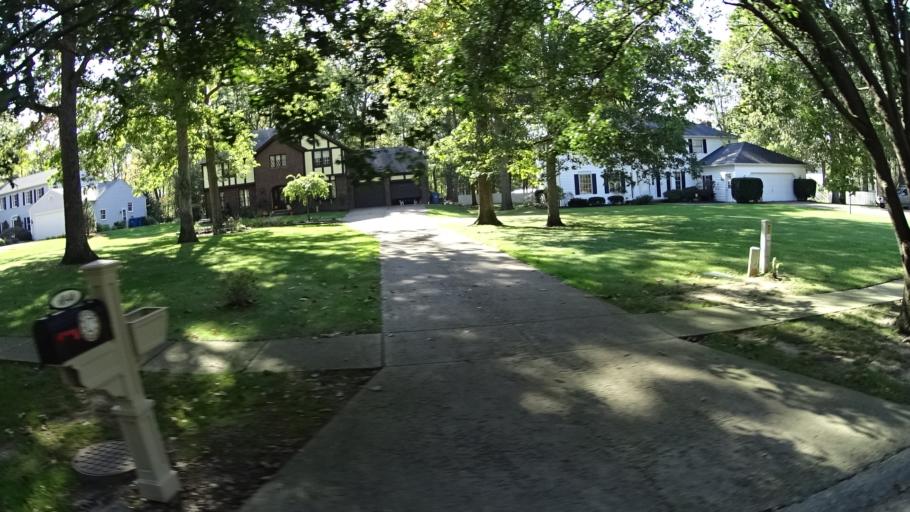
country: US
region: Ohio
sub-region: Lorain County
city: Vermilion-on-the-Lake
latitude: 41.4061
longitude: -82.3366
